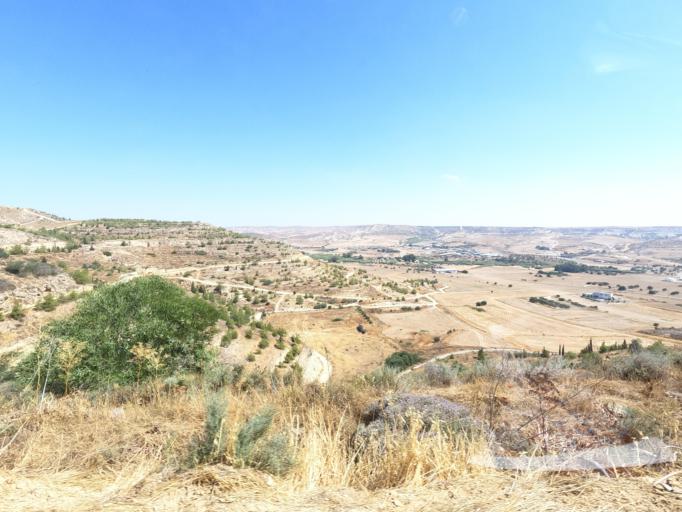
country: CY
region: Larnaka
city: Voroklini
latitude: 34.9919
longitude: 33.6500
